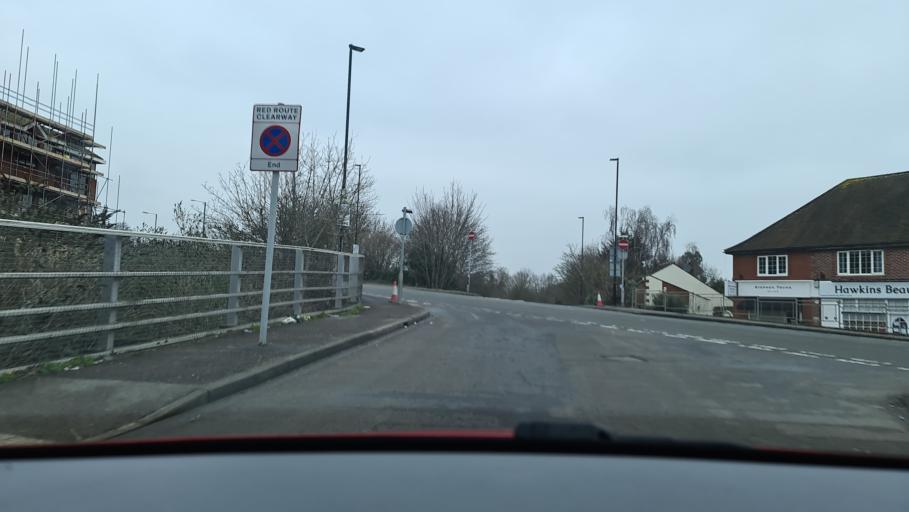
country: GB
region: England
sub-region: Greater London
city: New Malden
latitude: 51.4145
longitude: -0.2493
